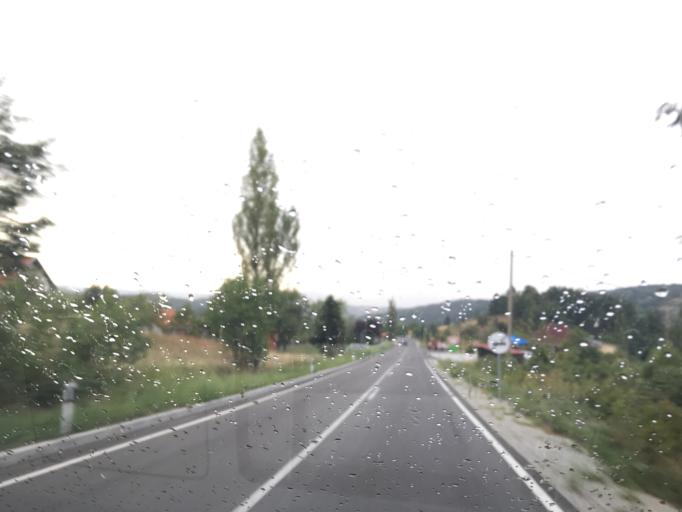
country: RS
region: Central Serbia
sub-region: Moravicki Okrug
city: Gornji Milanovac
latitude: 44.1265
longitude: 20.4872
